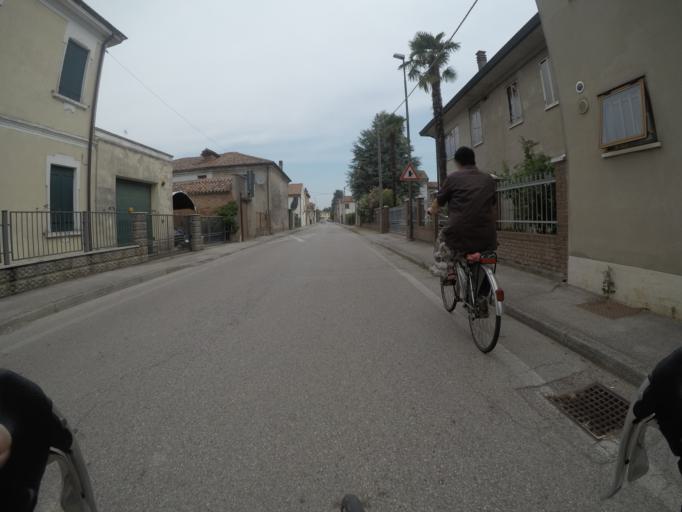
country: IT
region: Veneto
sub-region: Provincia di Rovigo
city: Costa di Rovigo
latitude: 45.0454
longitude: 11.6938
